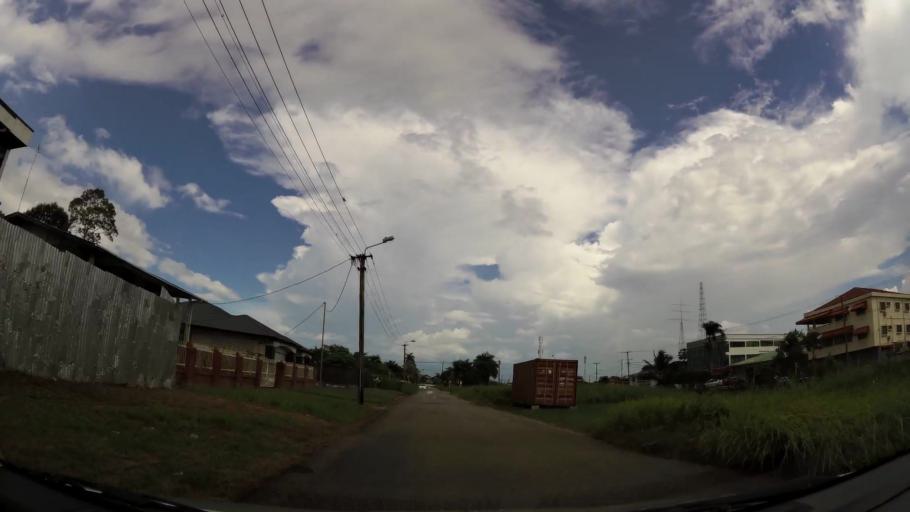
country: SR
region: Paramaribo
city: Paramaribo
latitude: 5.8371
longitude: -55.1336
